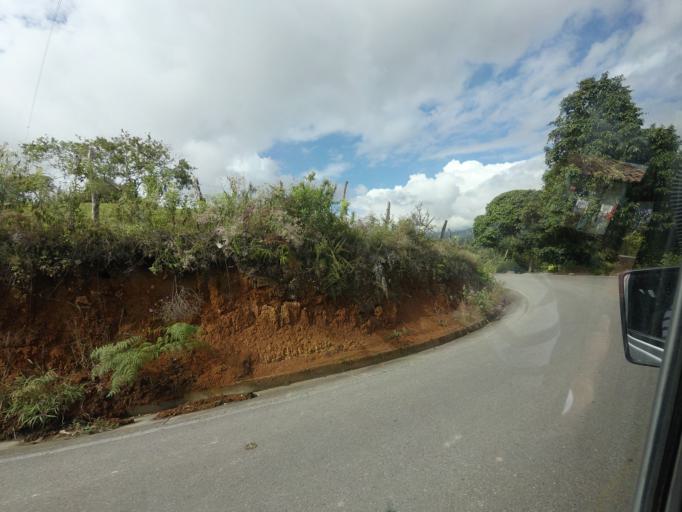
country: CO
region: Huila
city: San Agustin
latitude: 1.9224
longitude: -76.2848
